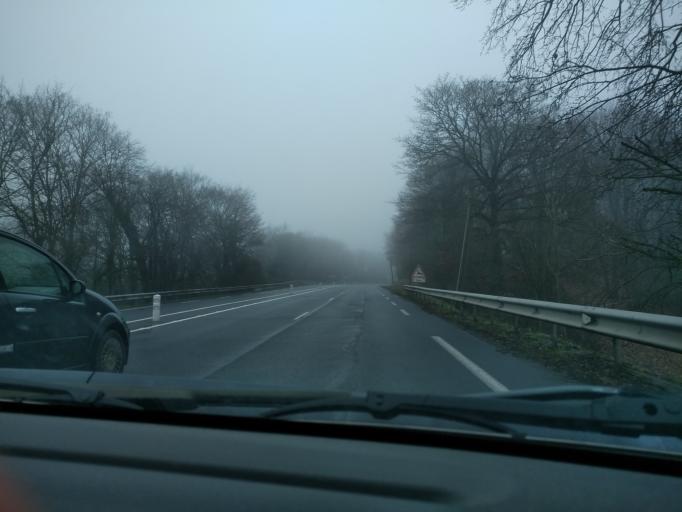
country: FR
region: Centre
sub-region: Departement d'Eure-et-Loir
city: Marboue
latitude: 48.1189
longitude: 1.3304
